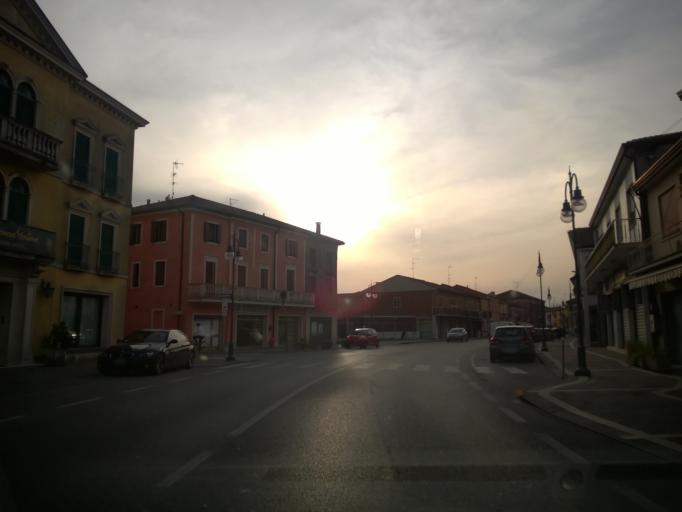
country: IT
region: Veneto
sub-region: Provincia di Padova
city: Casale di Scodosia
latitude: 45.1874
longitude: 11.4680
